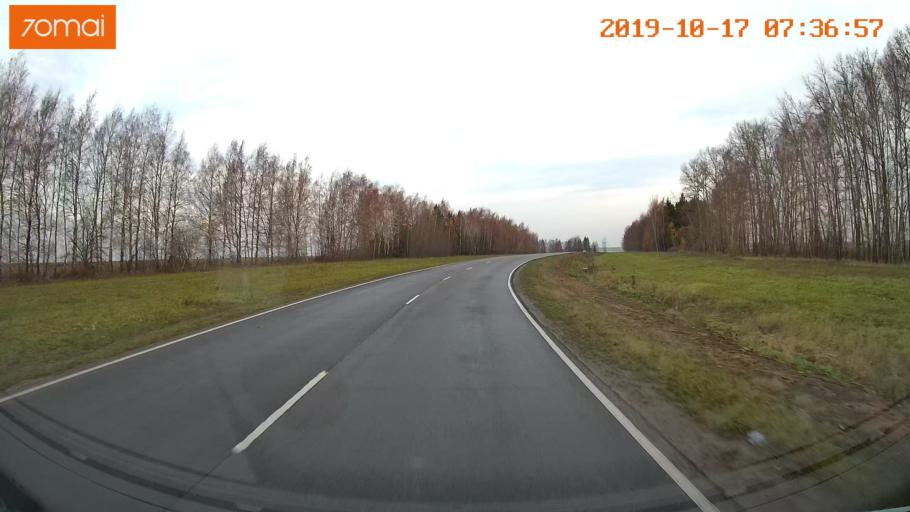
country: RU
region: Vladimir
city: Yur'yev-Pol'skiy
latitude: 56.4447
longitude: 39.9076
